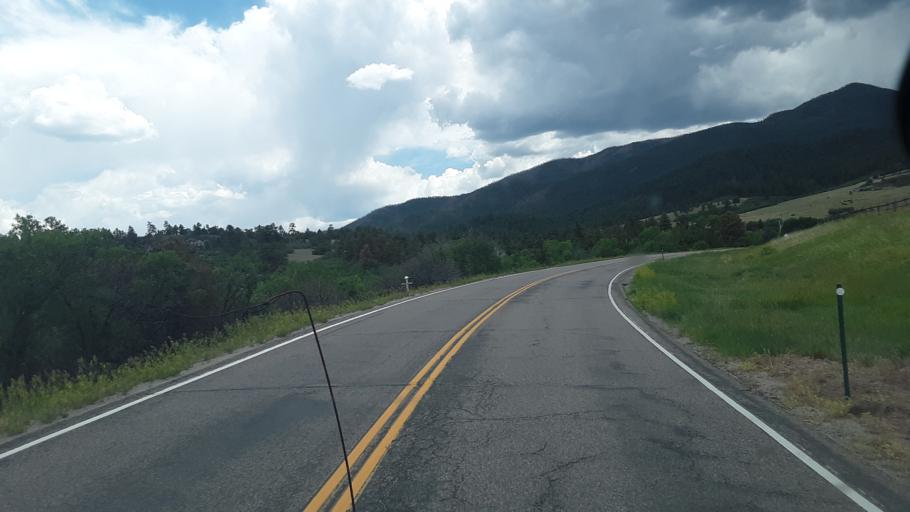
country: US
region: Colorado
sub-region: Fremont County
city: Florence
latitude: 38.1860
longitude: -105.1047
